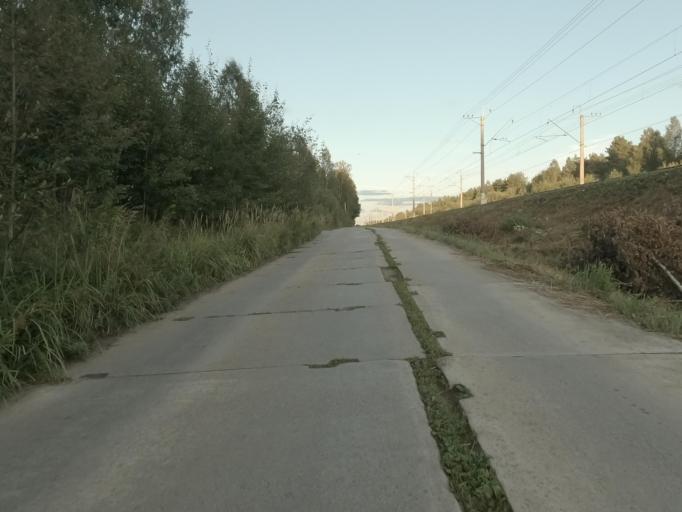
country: RU
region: Leningrad
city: Mga
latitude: 59.7626
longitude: 30.9965
